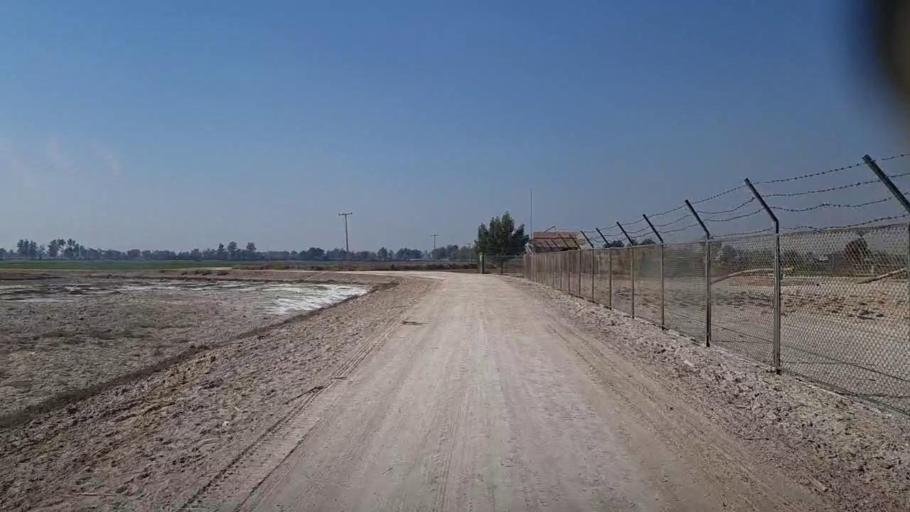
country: PK
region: Sindh
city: Khairpur
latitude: 28.0233
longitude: 69.7410
